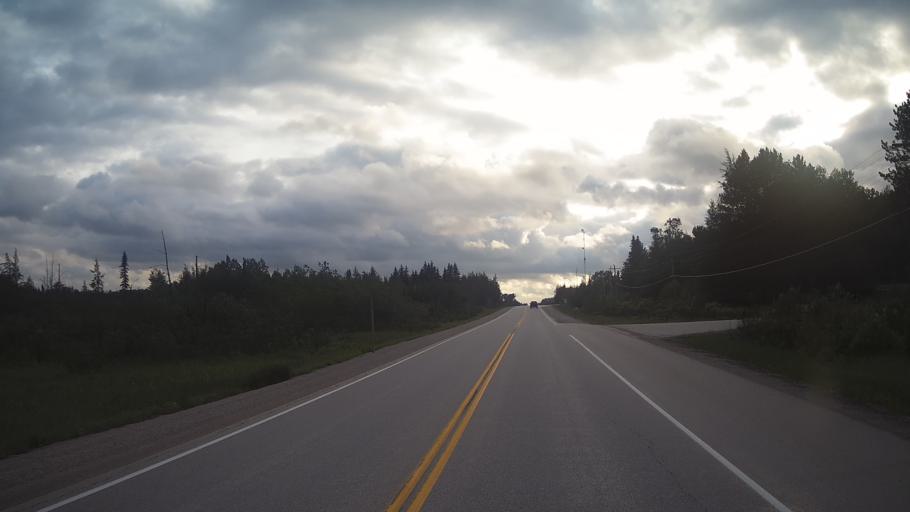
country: CA
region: Ontario
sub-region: Rainy River District
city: Atikokan
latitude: 49.0509
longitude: -90.4762
